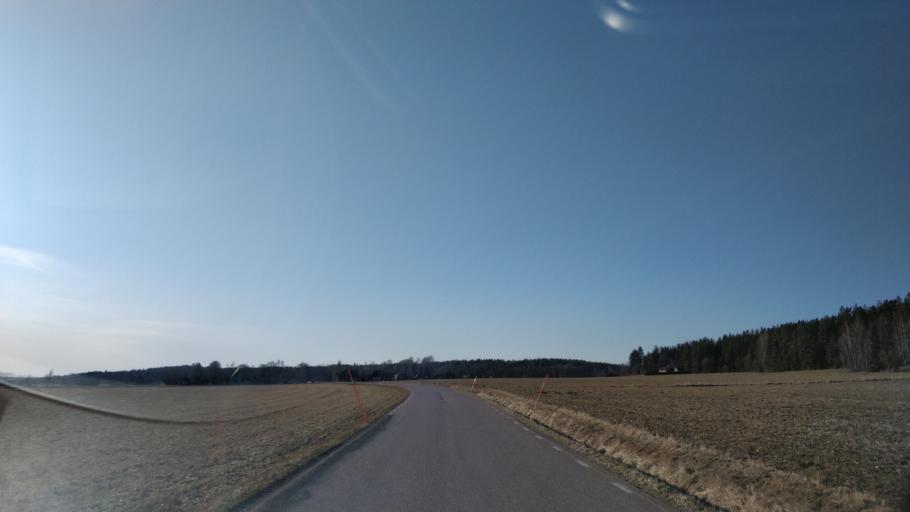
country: SE
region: Uppsala
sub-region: Enkopings Kommun
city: Orsundsbro
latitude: 59.7489
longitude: 17.1857
